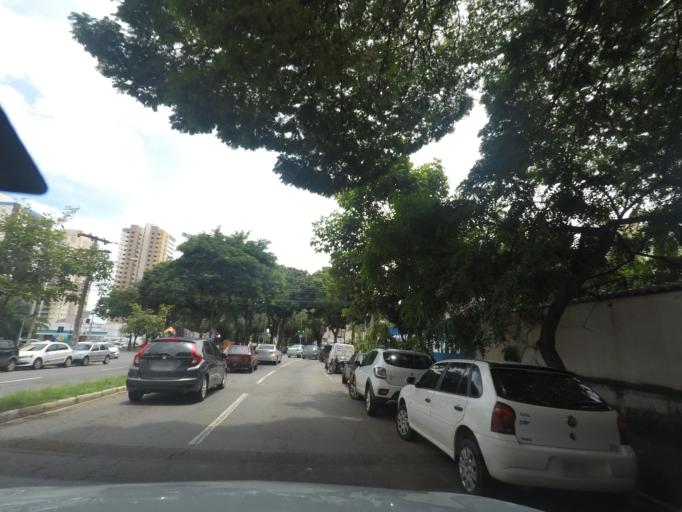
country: BR
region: Goias
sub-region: Goiania
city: Goiania
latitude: -16.6927
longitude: -49.2777
